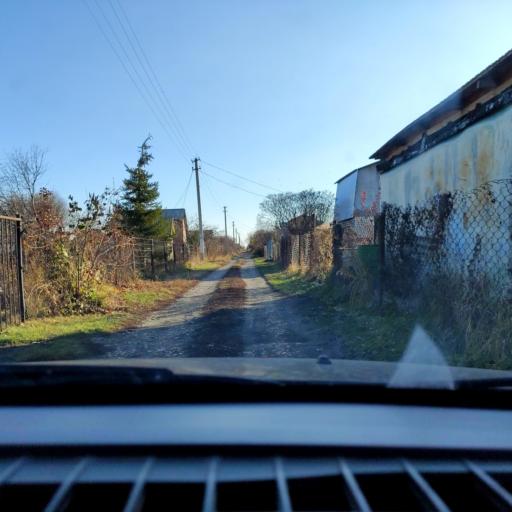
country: RU
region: Samara
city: Tol'yatti
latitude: 53.6619
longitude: 49.3415
